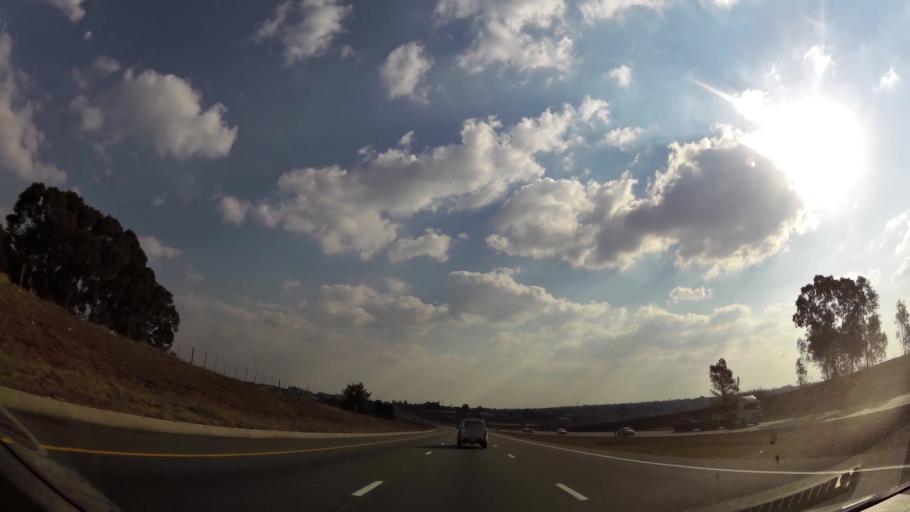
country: ZA
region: Gauteng
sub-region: Ekurhuleni Metropolitan Municipality
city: Germiston
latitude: -26.2518
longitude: 28.2083
